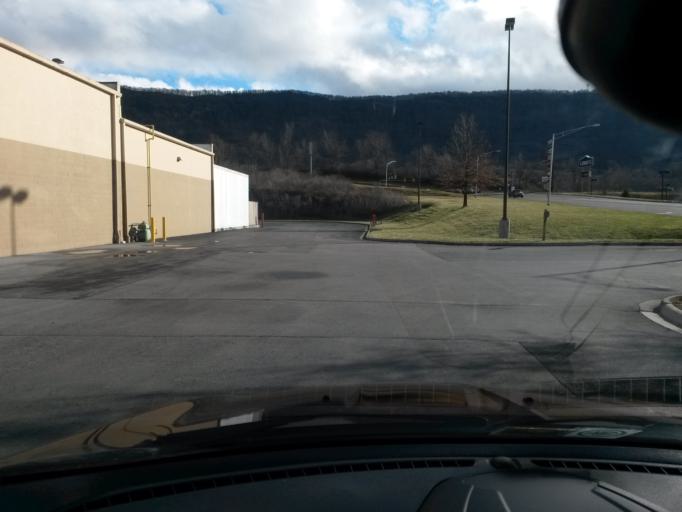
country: US
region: Virginia
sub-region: Tazewell County
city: Bluefield
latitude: 37.2394
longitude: -81.2489
